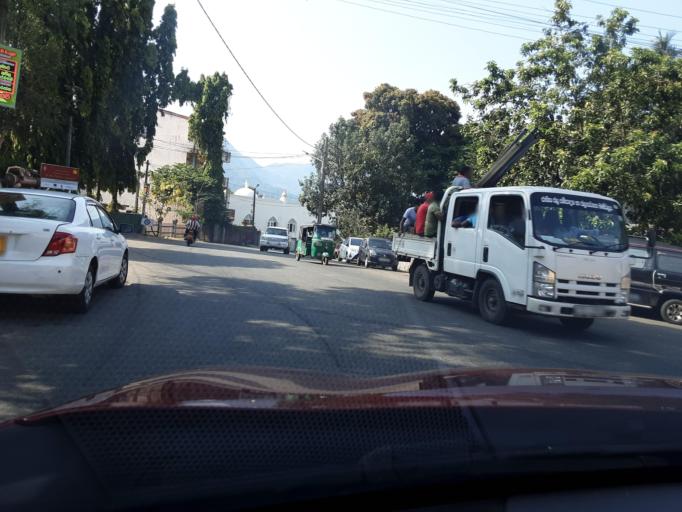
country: LK
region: Uva
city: Badulla
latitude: 6.9900
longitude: 81.0593
